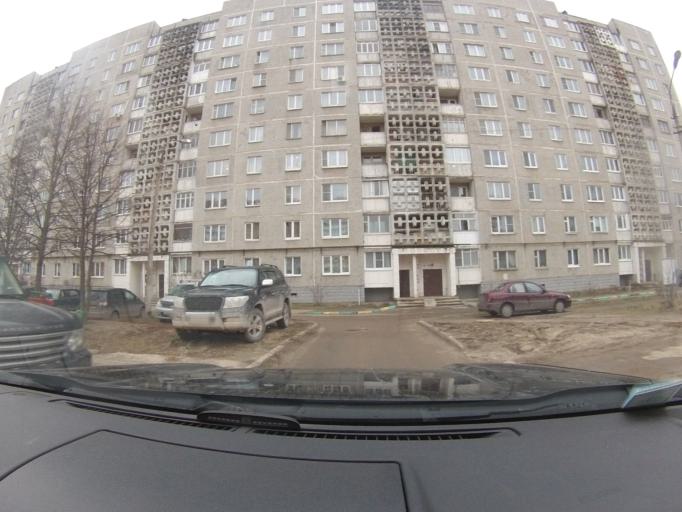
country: RU
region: Moskovskaya
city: Peski
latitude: 55.2751
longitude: 38.7566
